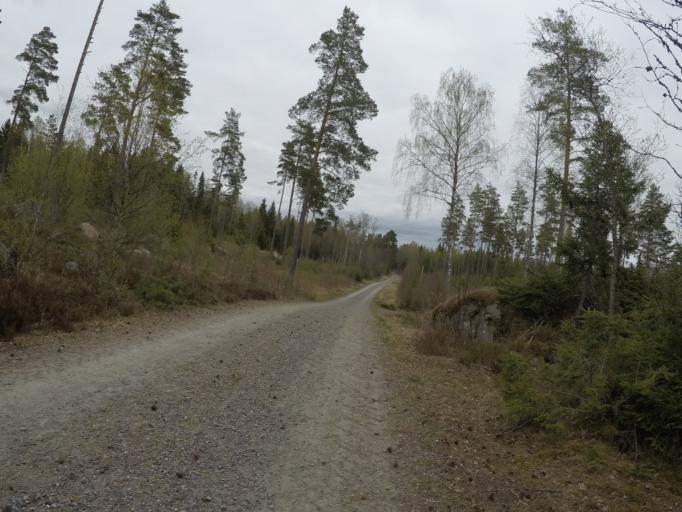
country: SE
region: Soedermanland
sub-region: Eskilstuna Kommun
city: Kvicksund
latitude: 59.4007
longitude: 16.2839
